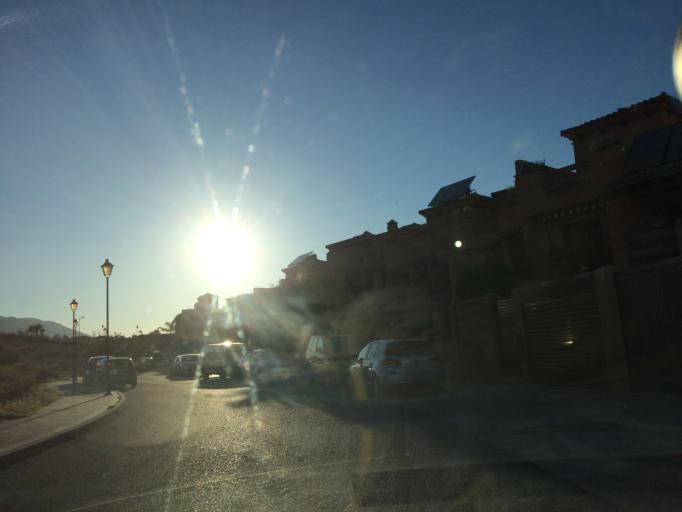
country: ES
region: Andalusia
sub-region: Provincia de Malaga
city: Alhaurin de la Torre
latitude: 36.6648
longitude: -4.5379
